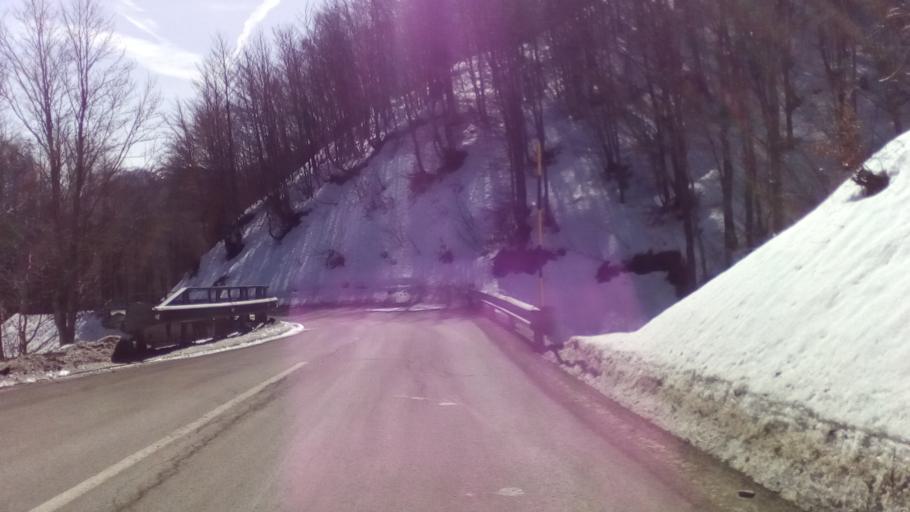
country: IT
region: Tuscany
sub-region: Provincia di Lucca
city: Castiglione di Garfagnana
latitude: 44.2075
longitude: 10.4890
